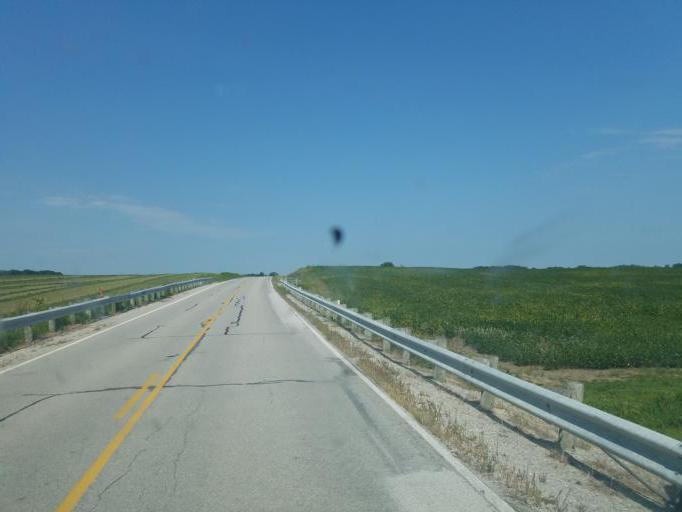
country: US
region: Ohio
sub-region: Marion County
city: Marion
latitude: 40.6782
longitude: -83.2345
